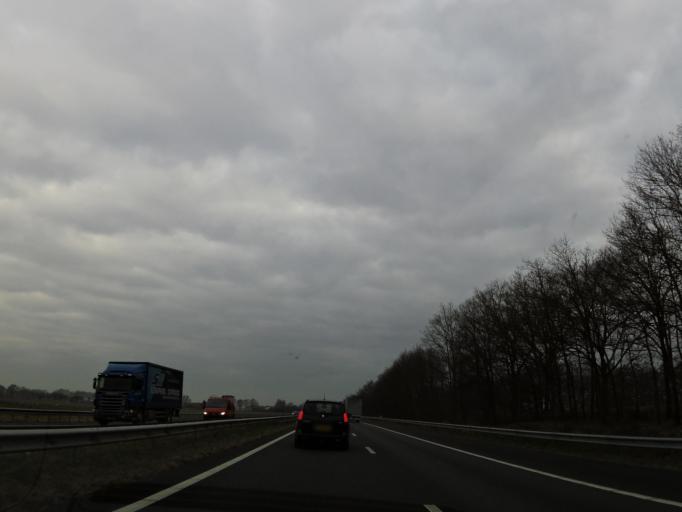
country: NL
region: Limburg
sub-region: Gemeente Leudal
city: Kelpen-Oler
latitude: 51.2061
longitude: 5.8238
